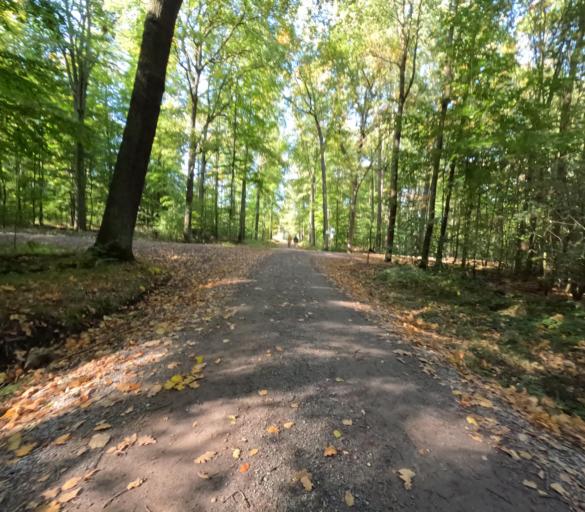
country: DE
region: Saxony
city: Moritzburg
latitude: 51.1694
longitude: 13.6675
